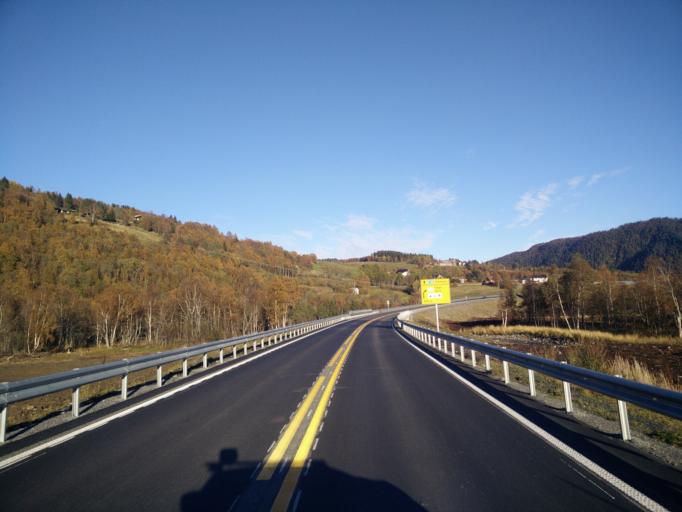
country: NO
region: Sor-Trondelag
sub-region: Snillfjord
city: Krokstadora
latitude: 63.2855
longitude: 9.6183
